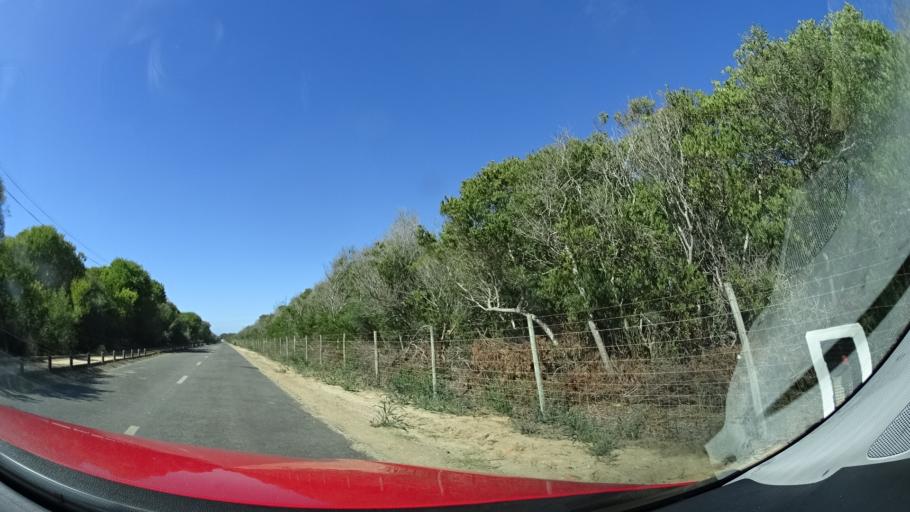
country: PT
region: Beja
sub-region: Odemira
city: Sao Teotonio
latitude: 37.5410
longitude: -8.7870
